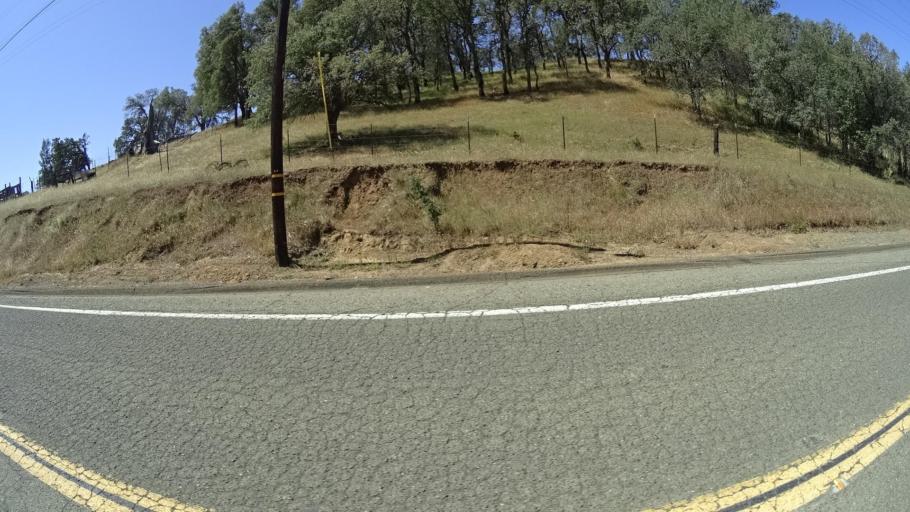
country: US
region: California
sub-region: Lake County
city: Lower Lake
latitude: 38.8968
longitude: -122.5542
